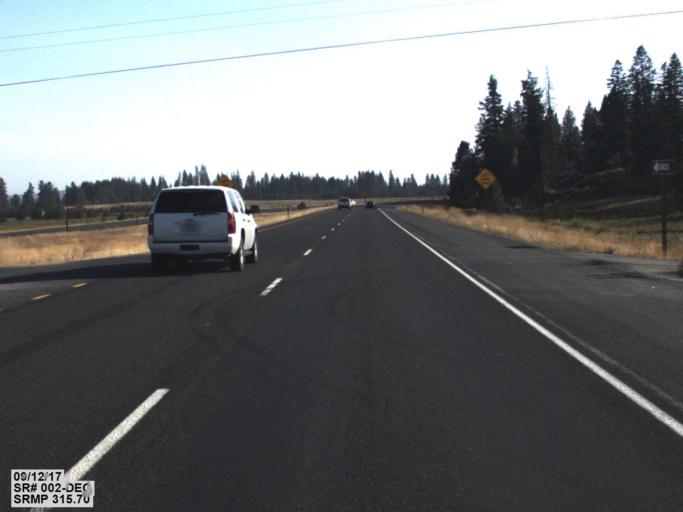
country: US
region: Washington
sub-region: Spokane County
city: Deer Park
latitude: 48.0499
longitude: -117.3441
